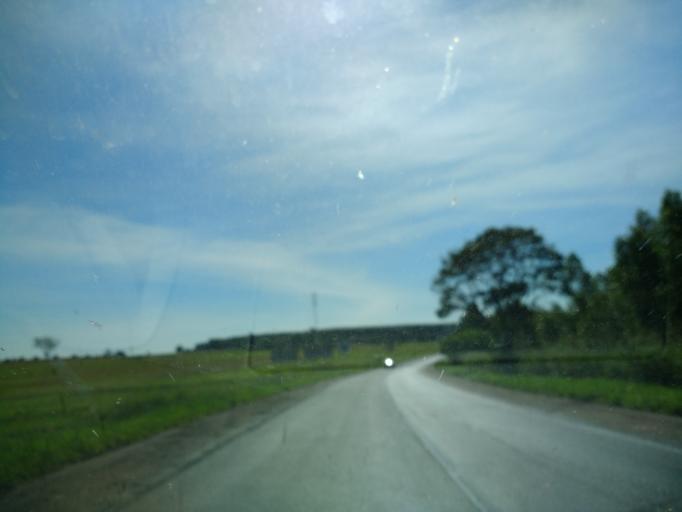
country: BR
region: Parana
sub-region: Umuarama
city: Umuarama
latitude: -23.8703
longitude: -53.3947
